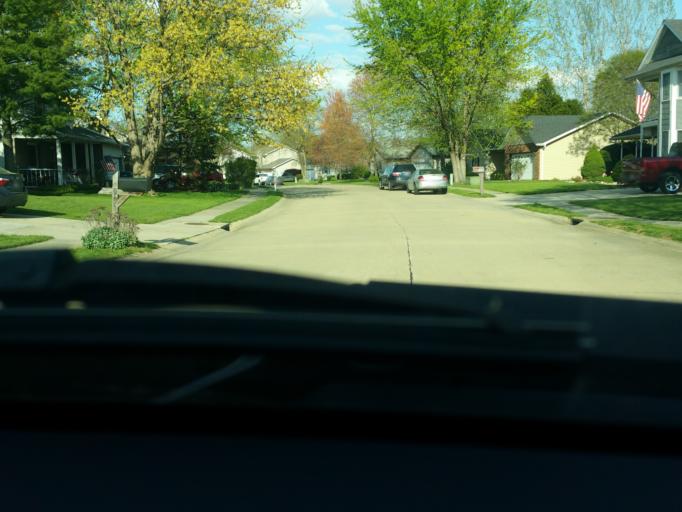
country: US
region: Illinois
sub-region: Madison County
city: Edwardsville
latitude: 38.7906
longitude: -89.9634
